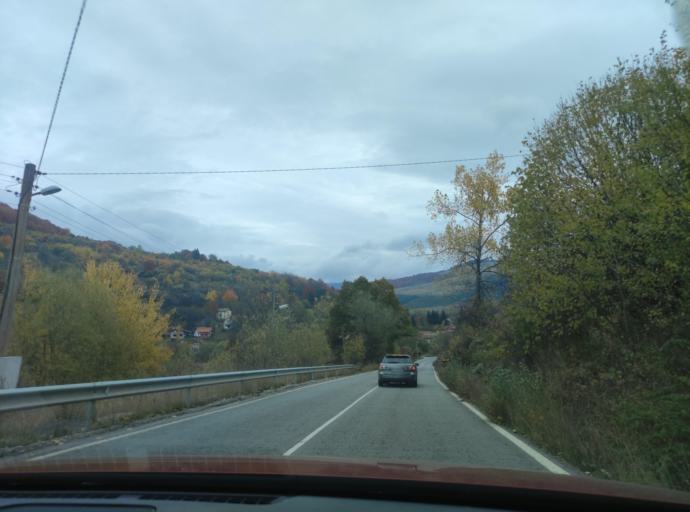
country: BG
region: Sofiya
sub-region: Obshtina Godech
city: Godech
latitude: 43.0678
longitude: 23.1079
